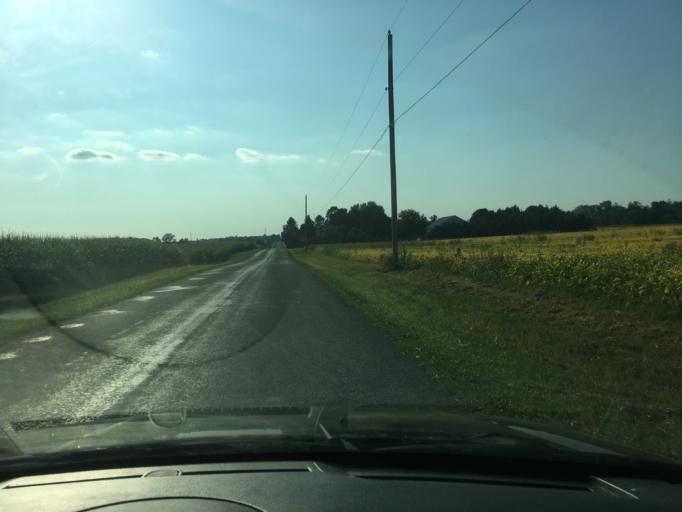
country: US
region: Ohio
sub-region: Logan County
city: West Liberty
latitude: 40.2882
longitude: -83.7643
